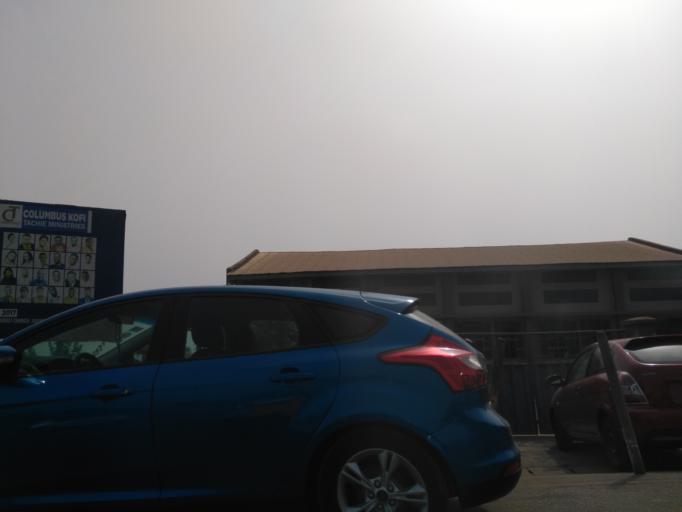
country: GH
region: Ashanti
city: Kumasi
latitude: 6.7020
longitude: -1.6078
